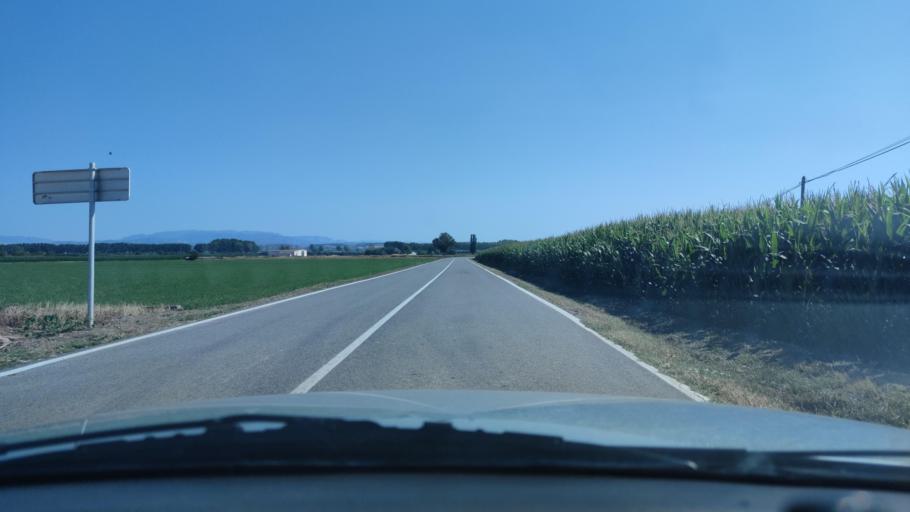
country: ES
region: Catalonia
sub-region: Provincia de Lleida
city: Linyola
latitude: 41.7193
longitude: 0.9156
